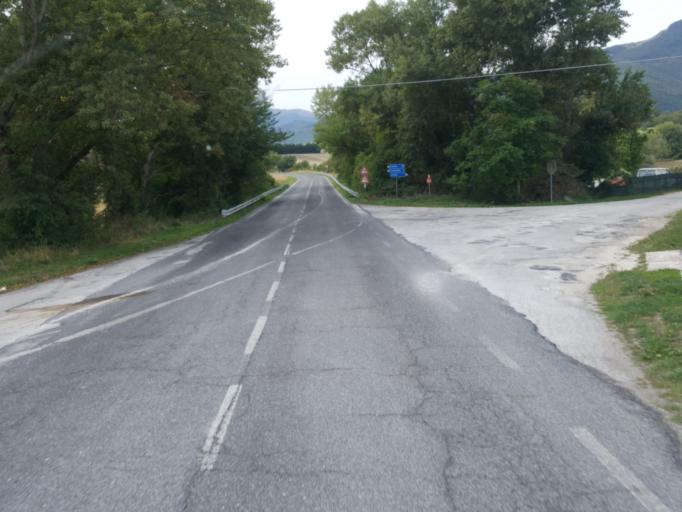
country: IT
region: The Marches
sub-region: Provincia di Ancona
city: Fabriano
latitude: 43.3463
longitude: 12.8293
